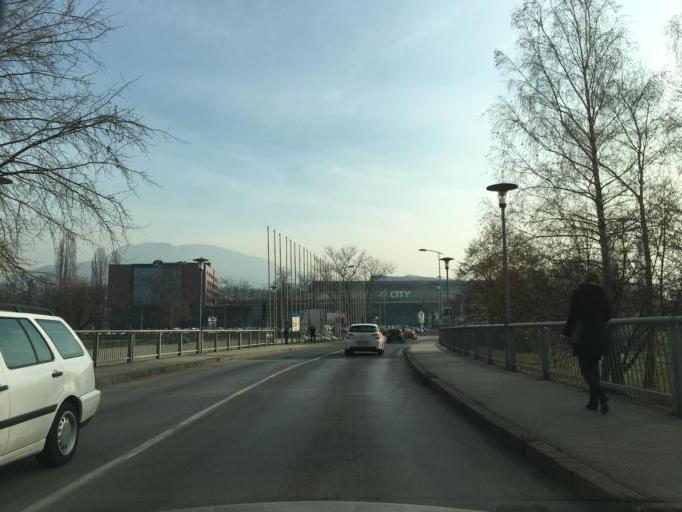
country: BA
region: Federation of Bosnia and Herzegovina
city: Zenica
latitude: 44.2035
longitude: 17.9095
